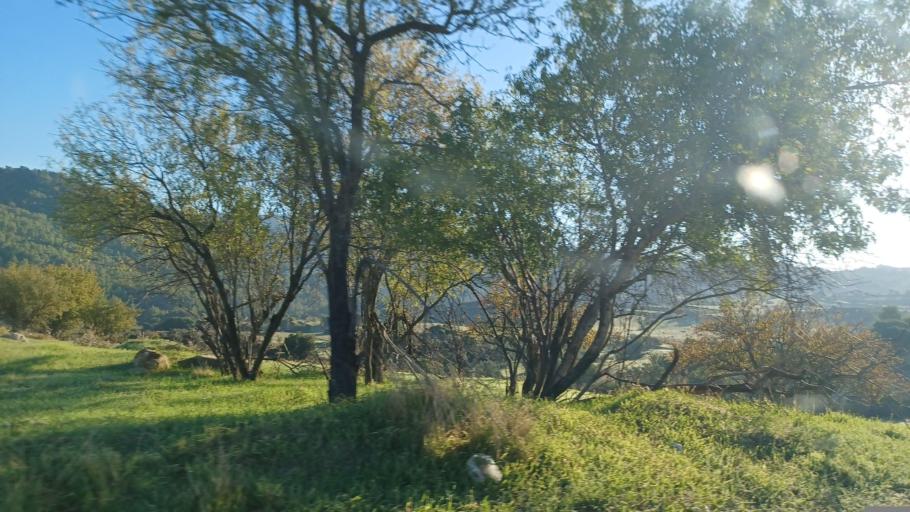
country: CY
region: Pafos
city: Polis
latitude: 34.9545
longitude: 32.5469
